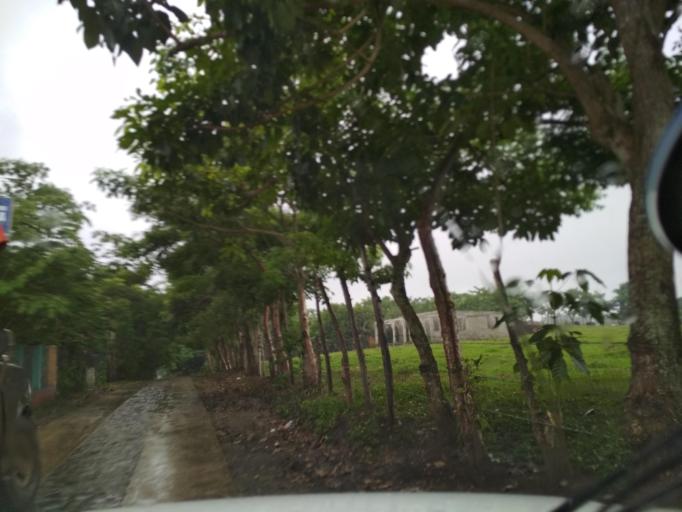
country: MX
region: Veracruz
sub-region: San Andres Tuxtla
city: Soyata
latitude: 18.4101
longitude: -95.2992
